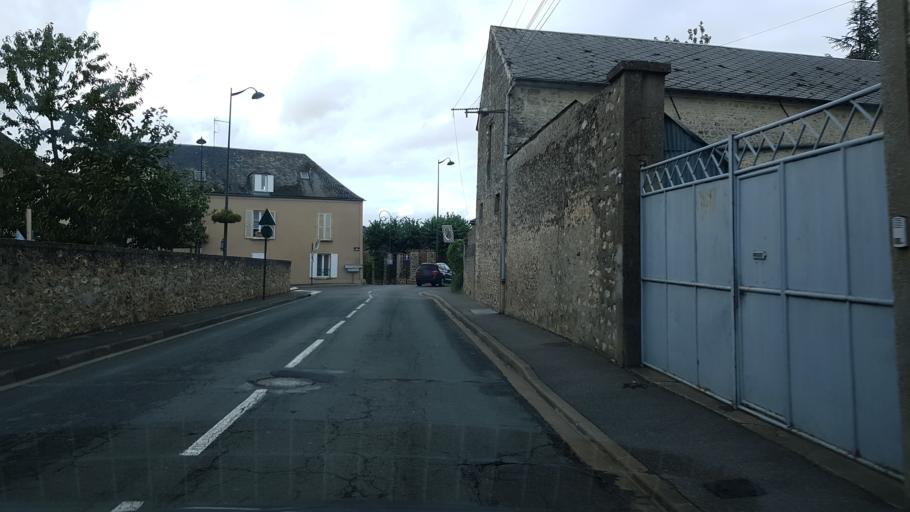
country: FR
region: Ile-de-France
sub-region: Departement de l'Essonne
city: Morigny-Champigny
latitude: 48.4287
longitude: 2.1731
